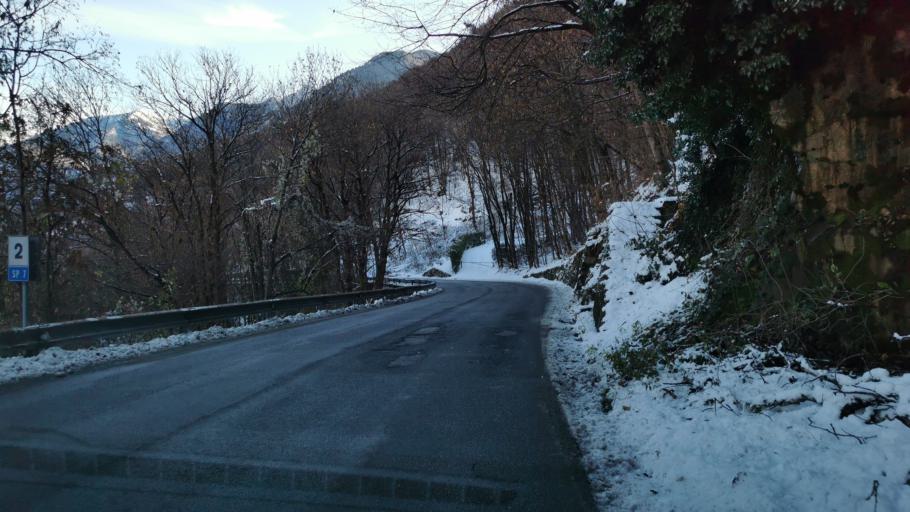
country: IT
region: Lombardy
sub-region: Provincia di Sondrio
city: Regoledo
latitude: 46.1262
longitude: 9.5417
